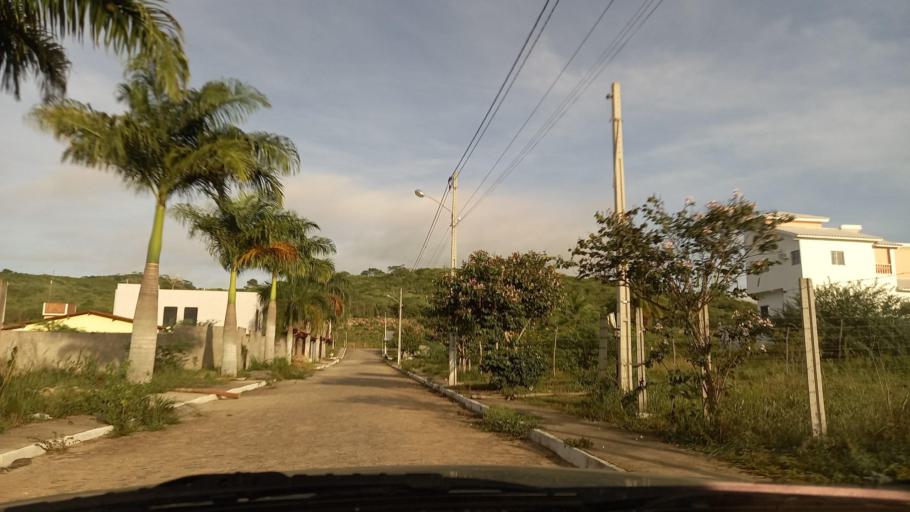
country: BR
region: Pernambuco
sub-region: Bezerros
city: Bezerros
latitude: -8.2169
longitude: -35.7516
